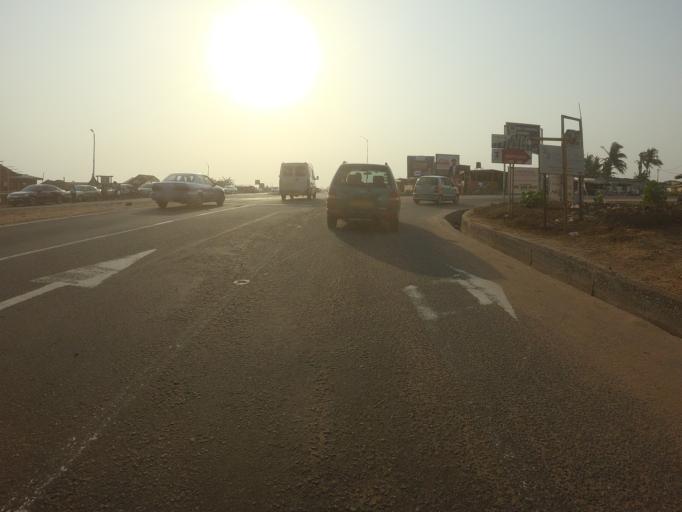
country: GH
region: Greater Accra
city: Nungua
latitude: 5.6114
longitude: -0.0460
